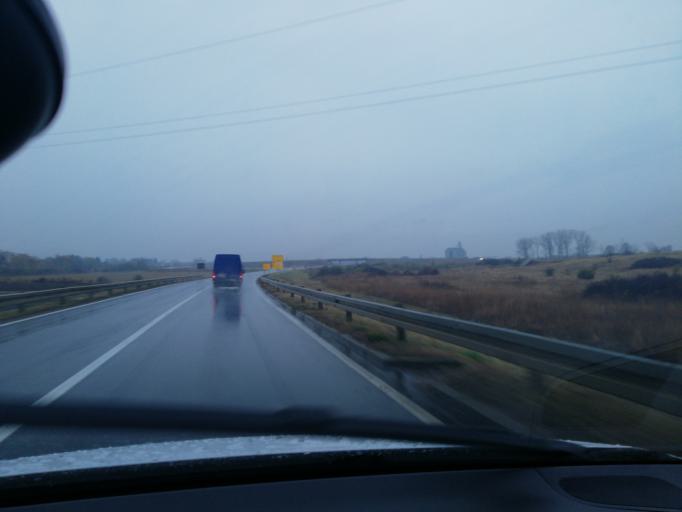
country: RS
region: Autonomna Pokrajina Vojvodina
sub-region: Sremski Okrug
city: Ruma
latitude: 45.0125
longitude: 19.8465
